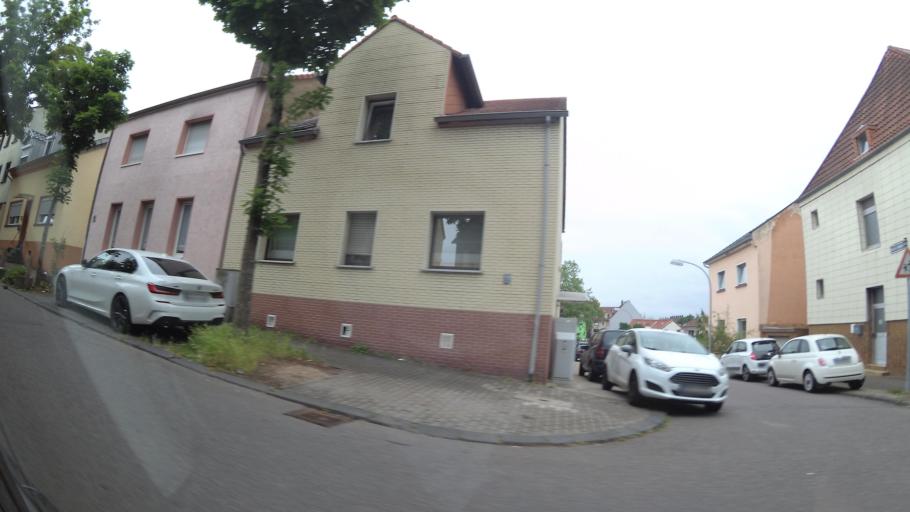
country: DE
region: Saarland
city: Saarbrucken
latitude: 49.2449
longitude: 6.9493
